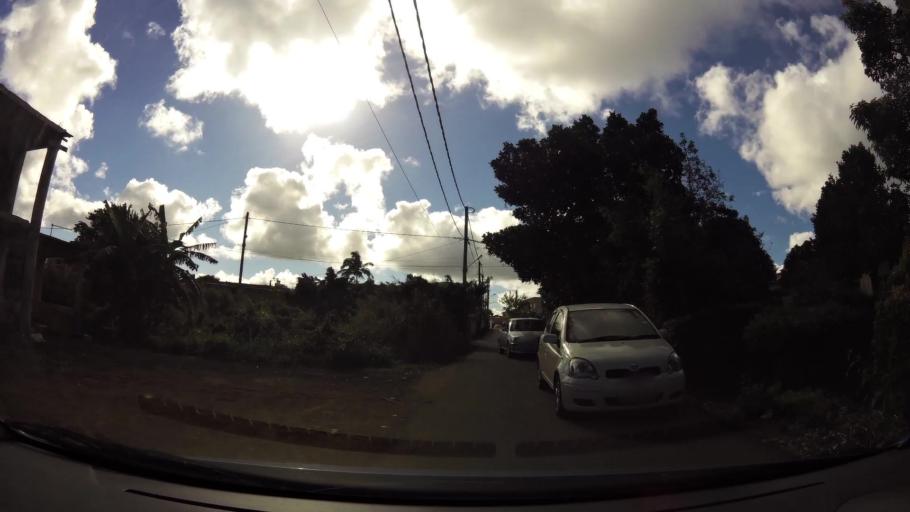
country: MU
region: Plaines Wilhems
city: Curepipe
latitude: -20.3029
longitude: 57.5173
